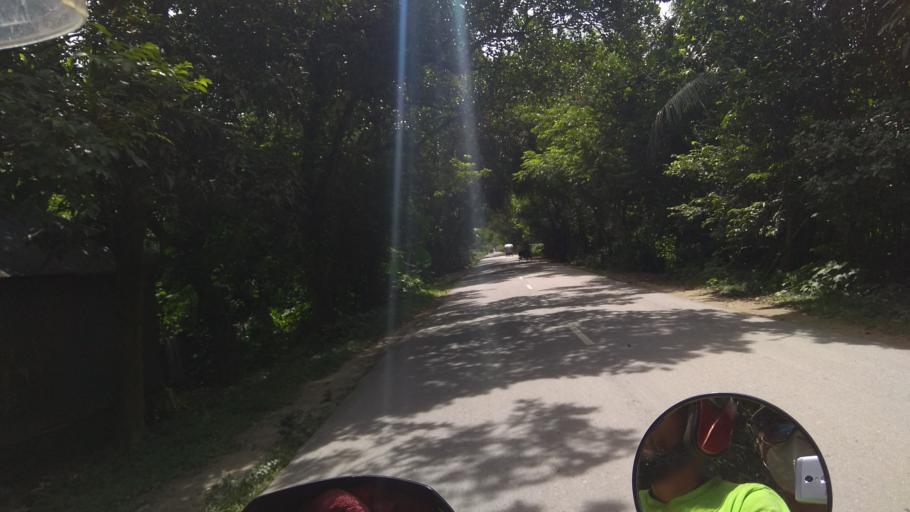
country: BD
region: Khulna
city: Kalia
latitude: 23.1956
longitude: 89.6813
